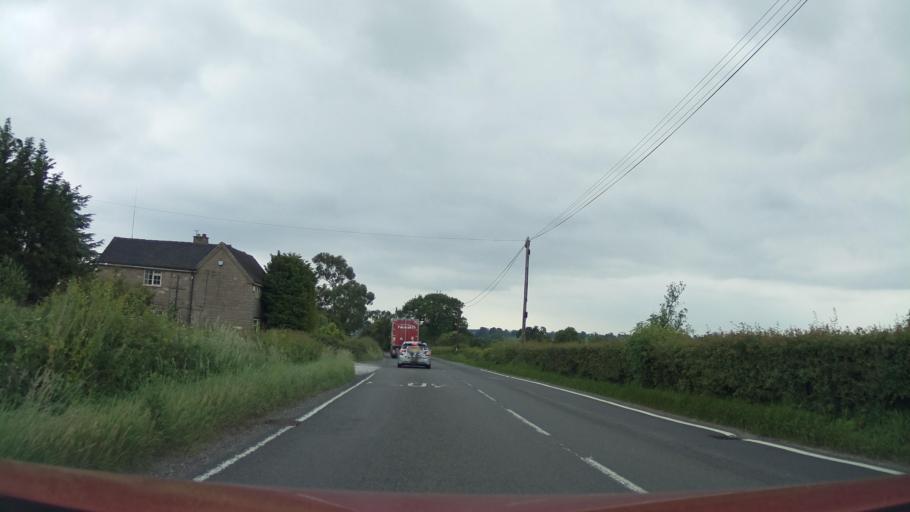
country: GB
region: England
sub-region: Staffordshire
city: Mayfield
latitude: 52.9506
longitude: -1.7581
